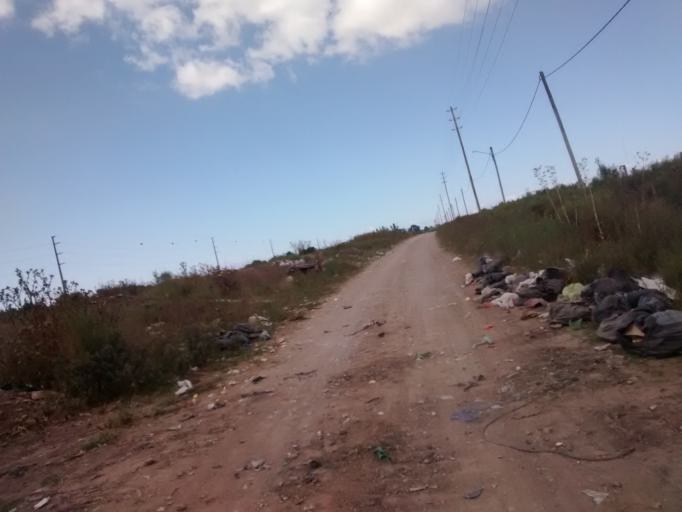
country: AR
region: Buenos Aires
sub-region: Partido de La Plata
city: La Plata
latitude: -34.9702
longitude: -57.9383
